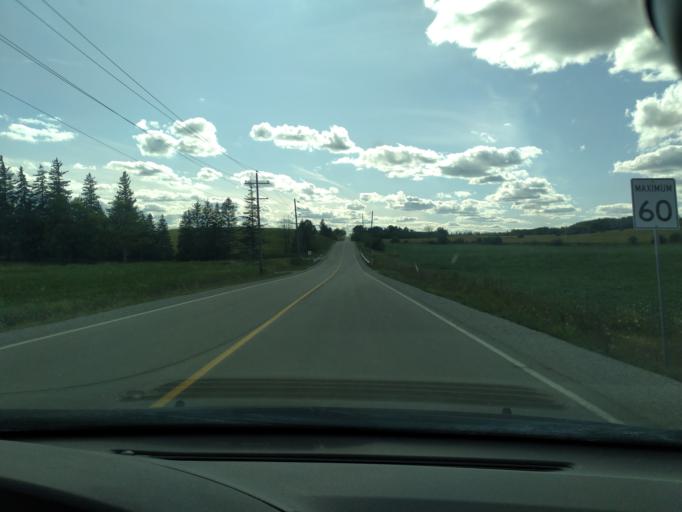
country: CA
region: Ontario
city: Bradford West Gwillimbury
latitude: 44.0837
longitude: -79.6439
